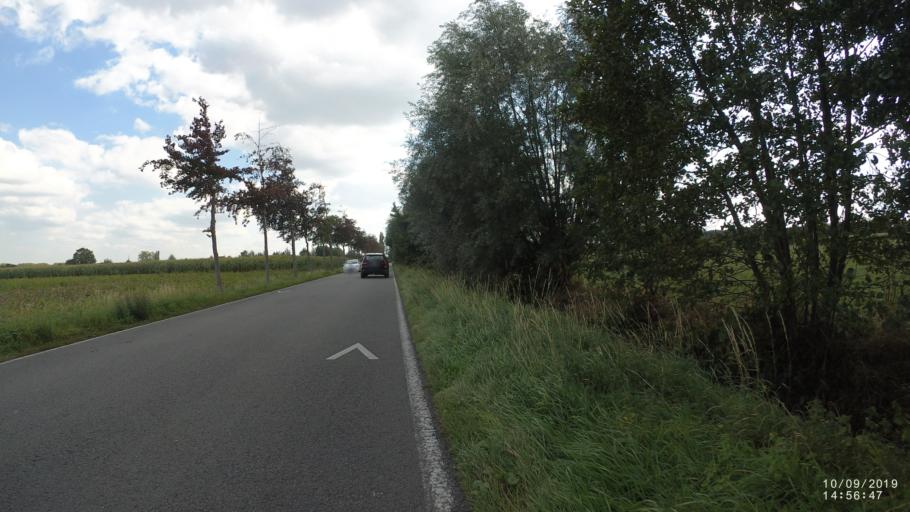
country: BE
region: Flanders
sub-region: Provincie Oost-Vlaanderen
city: Evergem
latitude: 51.1355
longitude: 3.7029
